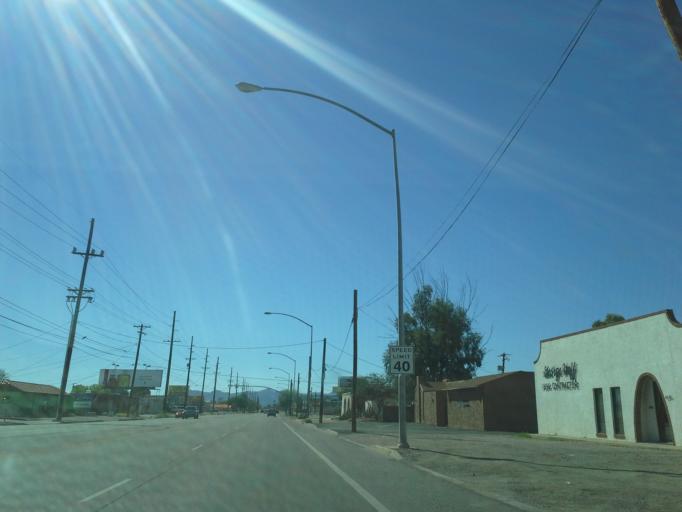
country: US
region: Arizona
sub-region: Pima County
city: Tucson
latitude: 32.2507
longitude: -110.9015
